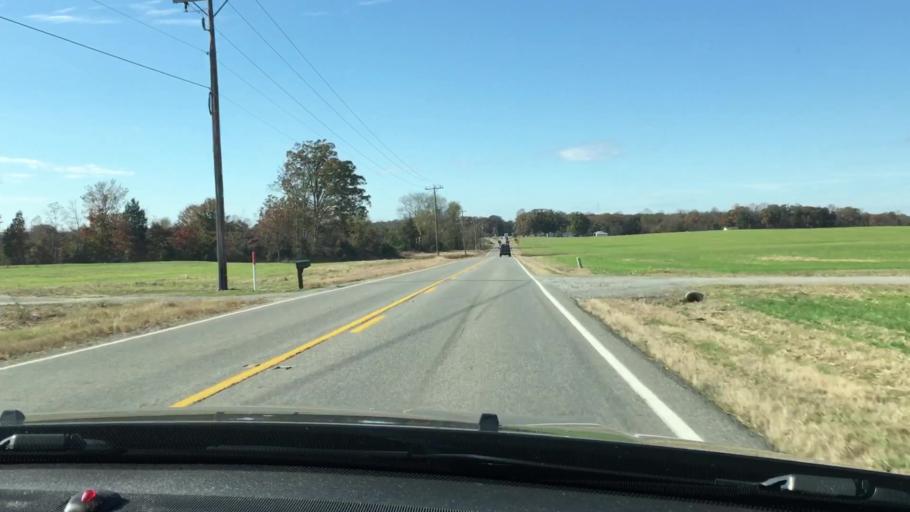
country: US
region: Virginia
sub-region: King William County
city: Central Garage
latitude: 37.7268
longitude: -77.0955
